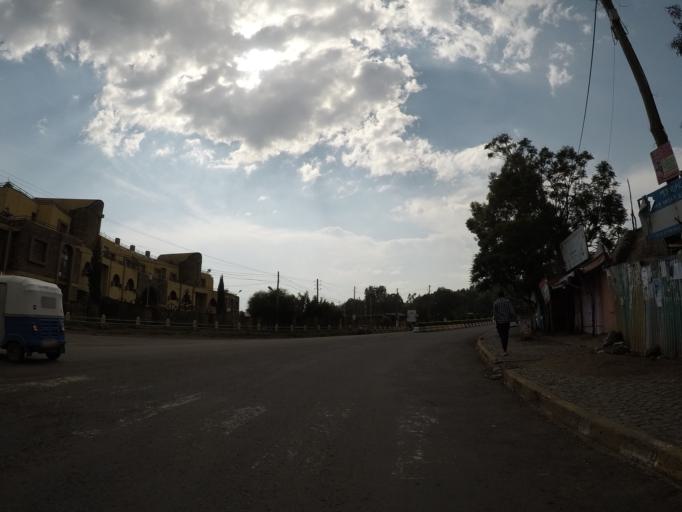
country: ET
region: Amhara
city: Gondar
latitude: 12.5910
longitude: 37.4441
